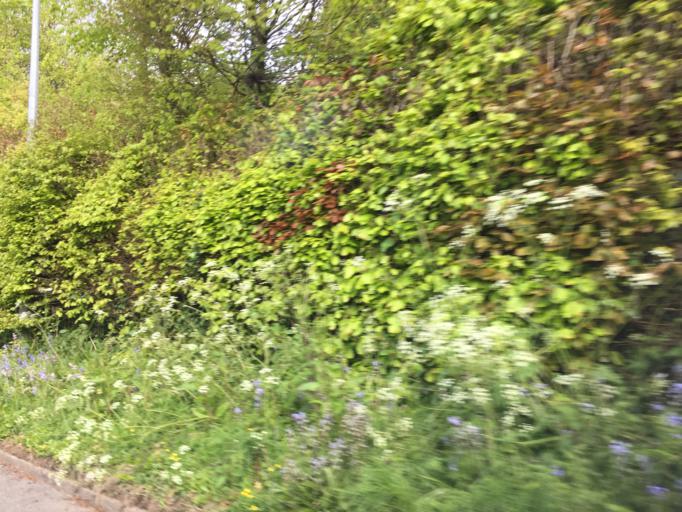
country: GB
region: Wales
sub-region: Cardiff
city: Radyr
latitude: 51.5293
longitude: -3.2263
